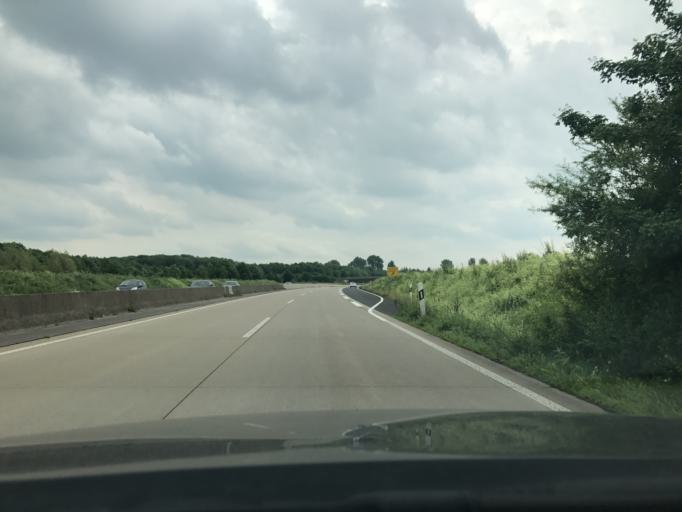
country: DE
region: North Rhine-Westphalia
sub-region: Regierungsbezirk Dusseldorf
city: Ratingen
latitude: 51.3103
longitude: 6.7737
